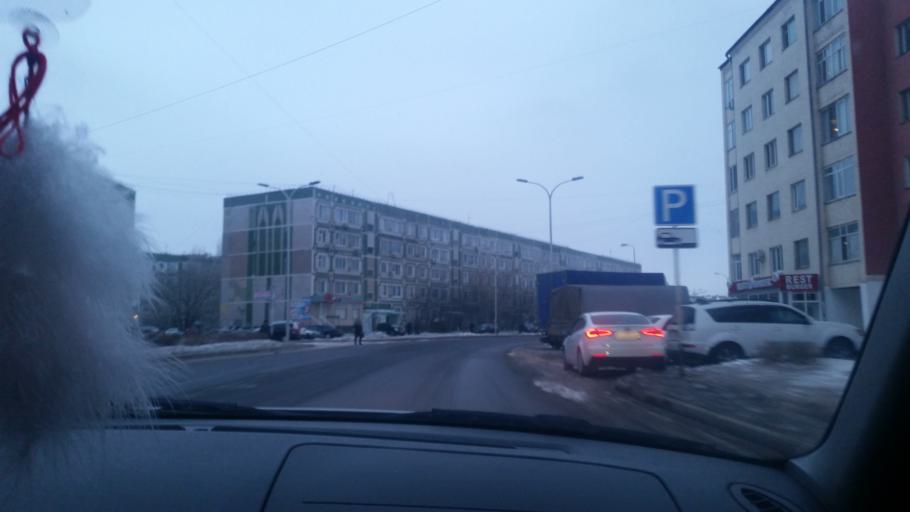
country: KZ
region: Astana Qalasy
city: Astana
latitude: 51.1460
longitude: 71.4707
